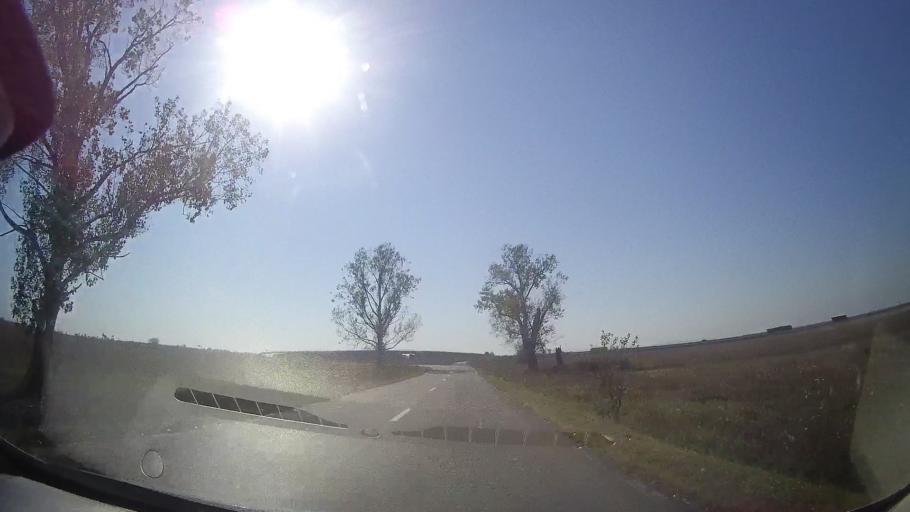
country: RO
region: Timis
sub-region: Comuna Ghizela
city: Ghizela
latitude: 45.7857
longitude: 21.7310
